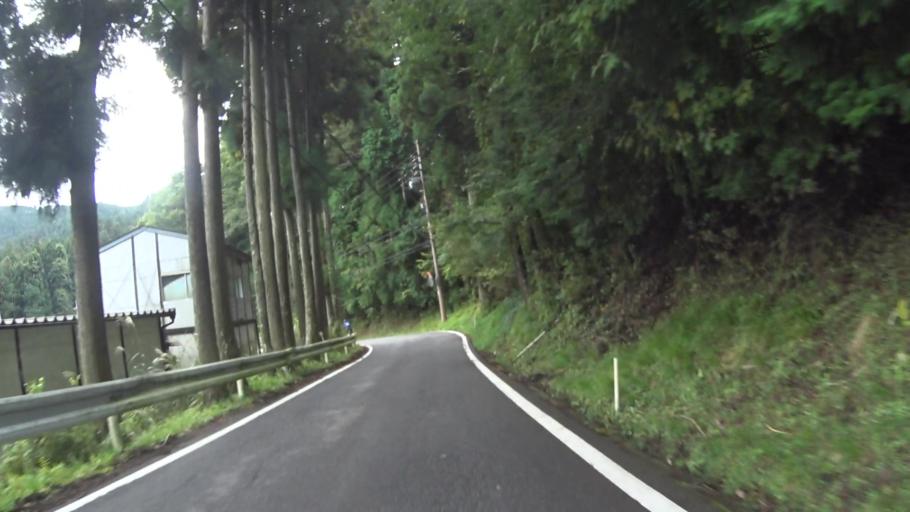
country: JP
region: Kyoto
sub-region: Kyoto-shi
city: Kamigyo-ku
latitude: 35.1637
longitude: 135.7776
